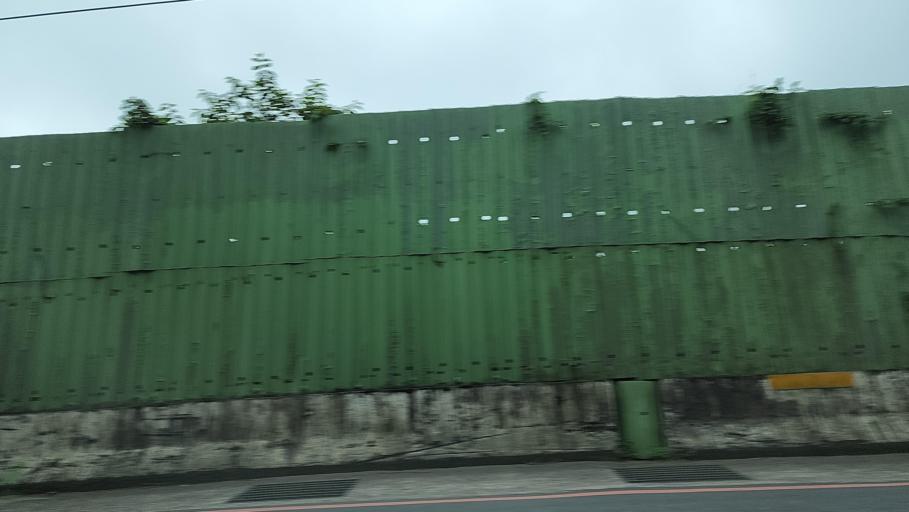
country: TW
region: Taiwan
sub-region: Keelung
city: Keelung
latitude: 25.1634
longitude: 121.6868
